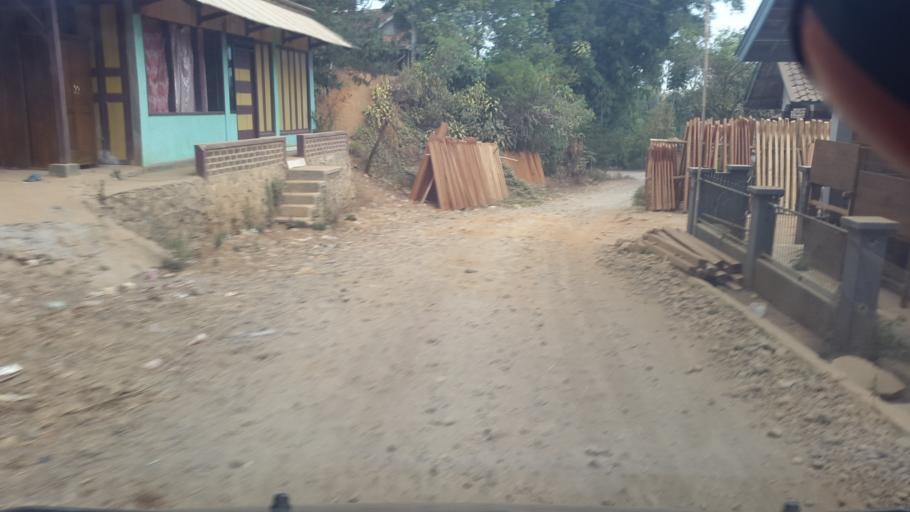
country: ID
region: West Java
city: Cisireum
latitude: -7.1131
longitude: 106.6465
